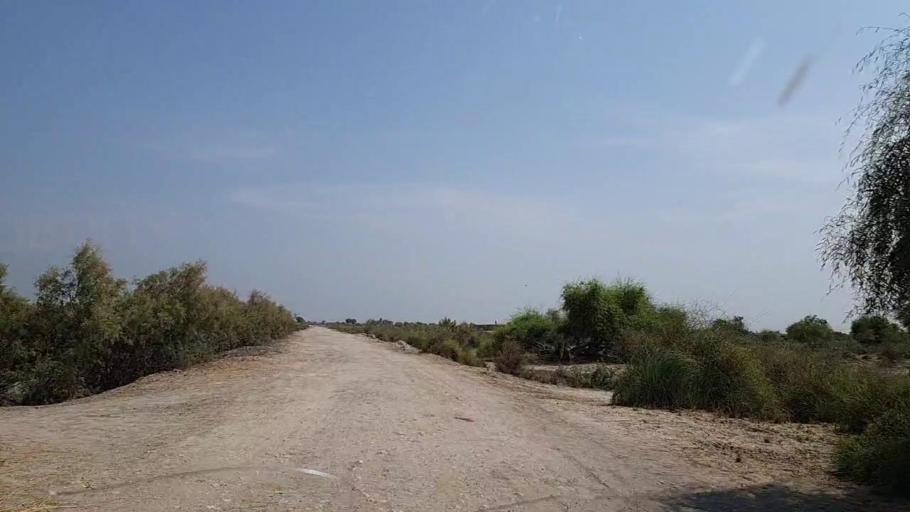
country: PK
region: Sindh
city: Khanpur
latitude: 27.8108
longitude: 69.3084
